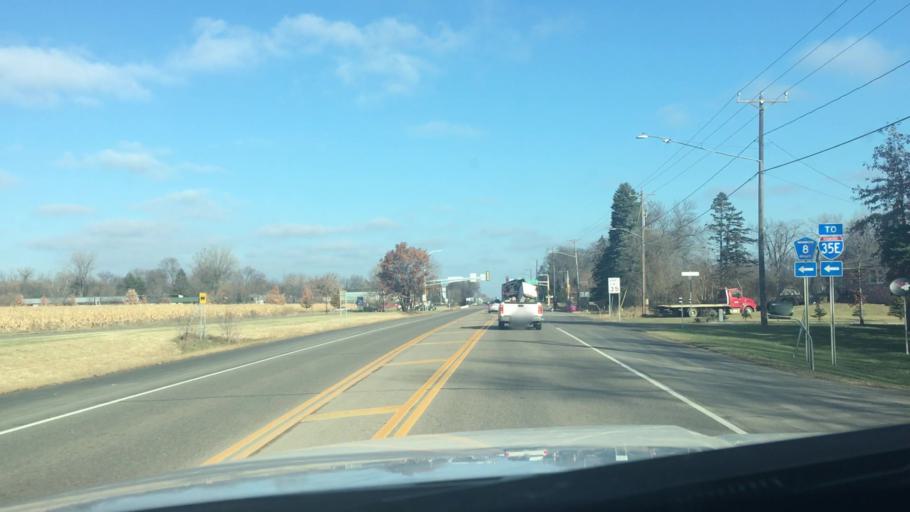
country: US
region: Minnesota
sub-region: Washington County
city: Hugo
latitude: 45.1554
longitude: -92.9945
